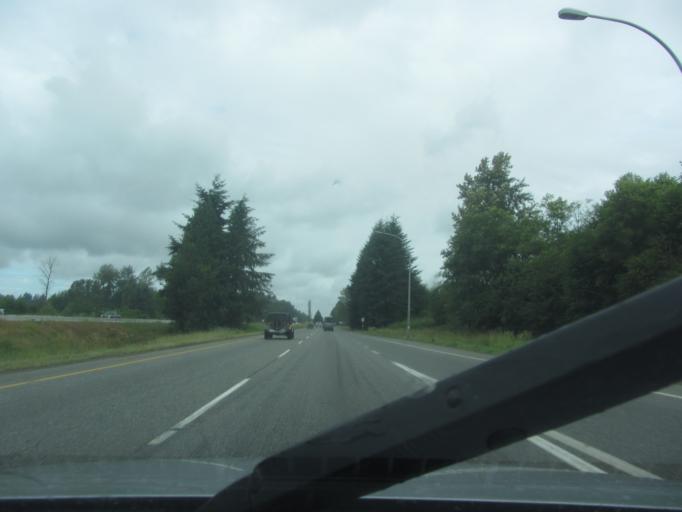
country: CA
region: British Columbia
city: Aldergrove
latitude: 49.1045
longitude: -122.4996
